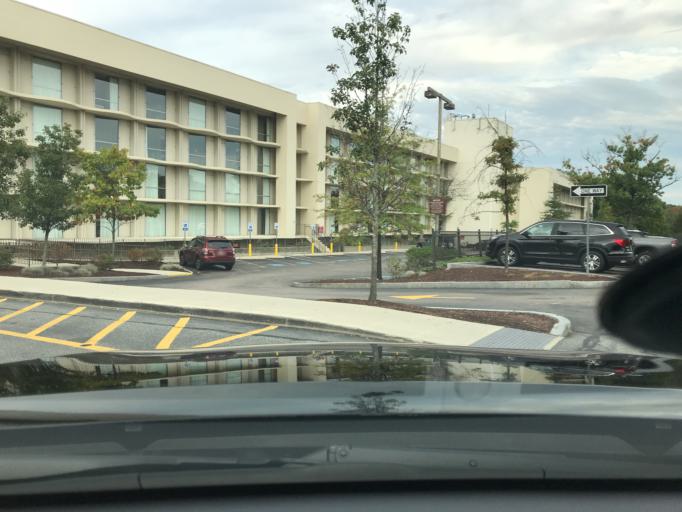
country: US
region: Massachusetts
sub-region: Middlesex County
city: Waltham
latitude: 42.3466
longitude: -71.2581
